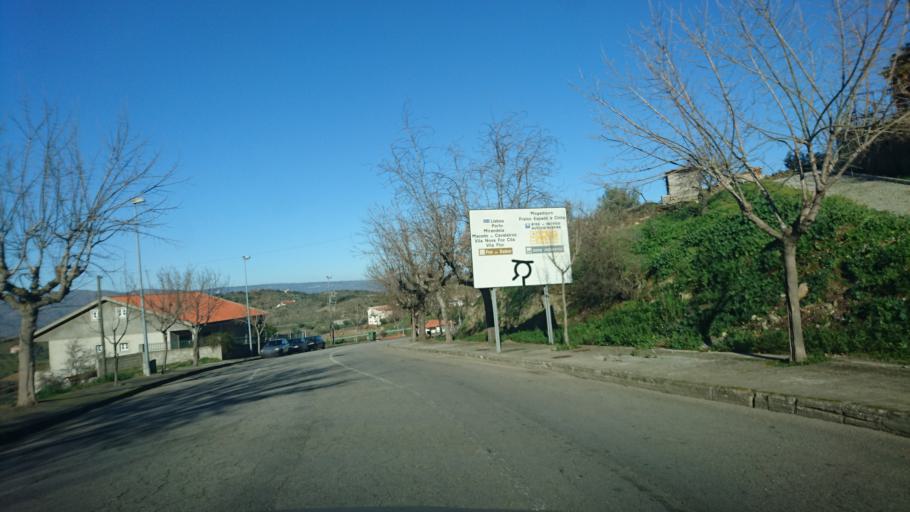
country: PT
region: Braganca
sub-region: Torre de Moncorvo
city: Torre de Moncorvo
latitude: 41.1772
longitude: -7.0536
